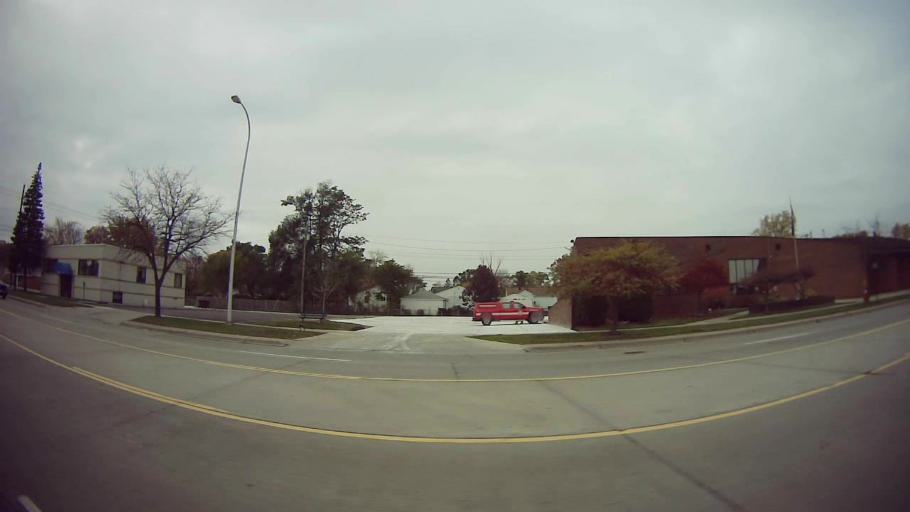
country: US
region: Michigan
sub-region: Oakland County
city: Madison Heights
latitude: 42.4843
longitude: -83.1051
